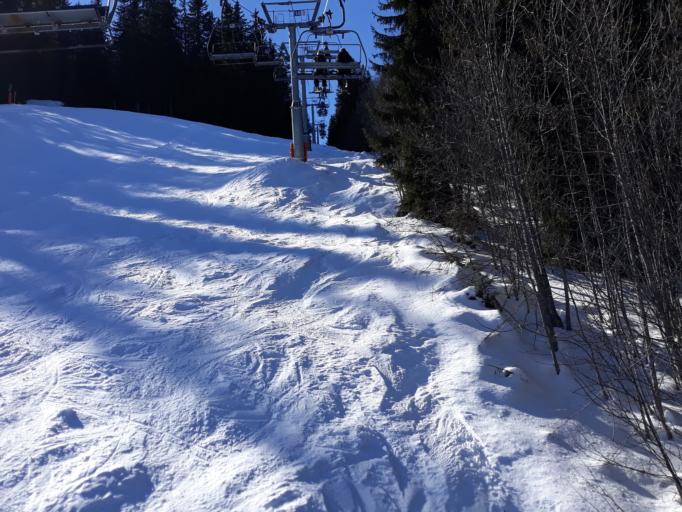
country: FR
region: Rhone-Alpes
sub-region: Departement de la Haute-Savoie
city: Combloux
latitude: 45.8850
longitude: 6.6118
